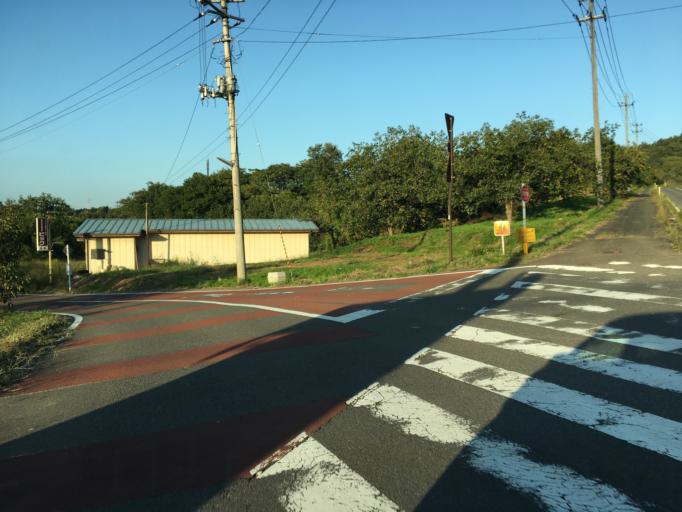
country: JP
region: Fukushima
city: Hobaramachi
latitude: 37.7923
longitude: 140.5367
